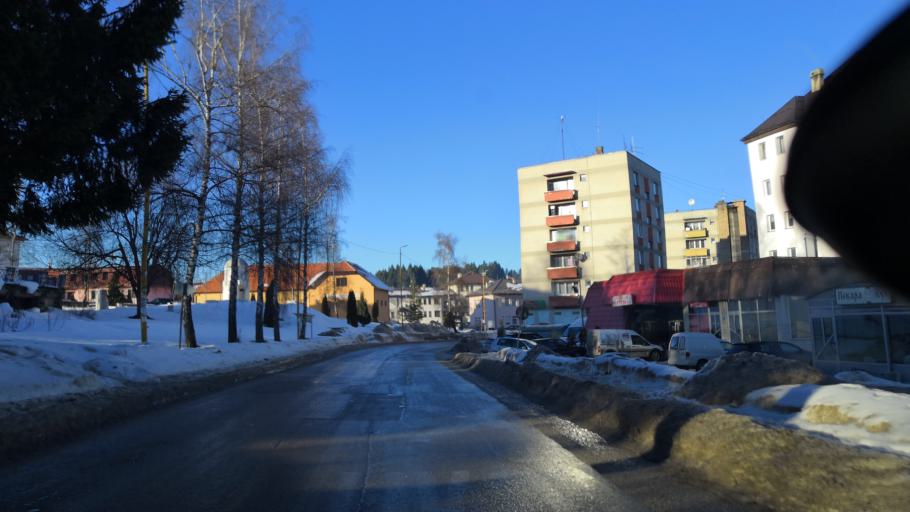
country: BA
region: Republika Srpska
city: Han Pijesak
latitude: 44.0803
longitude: 18.9521
